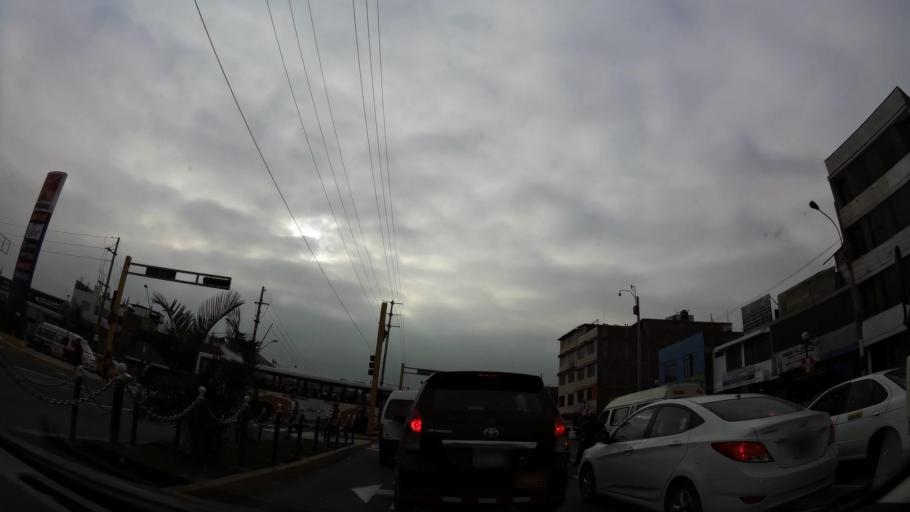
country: PE
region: Lima
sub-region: Lima
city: Surco
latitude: -12.1904
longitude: -77.0062
